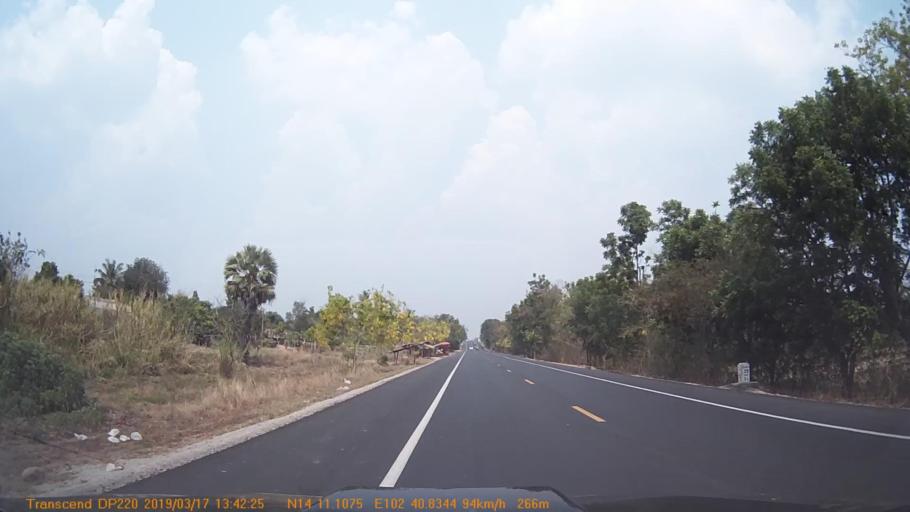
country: TH
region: Buriram
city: Non Din Daeng
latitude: 14.1852
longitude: 102.6807
